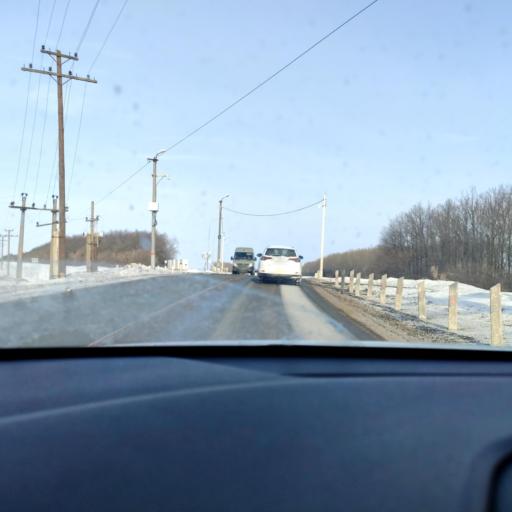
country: RU
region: Tatarstan
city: Buinsk
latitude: 54.9027
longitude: 48.2710
